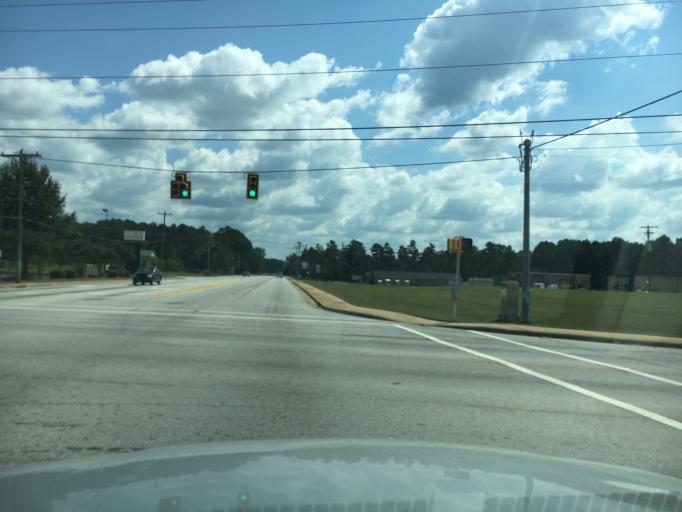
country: US
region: South Carolina
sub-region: Greenwood County
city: Greenwood
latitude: 34.2029
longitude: -82.1993
